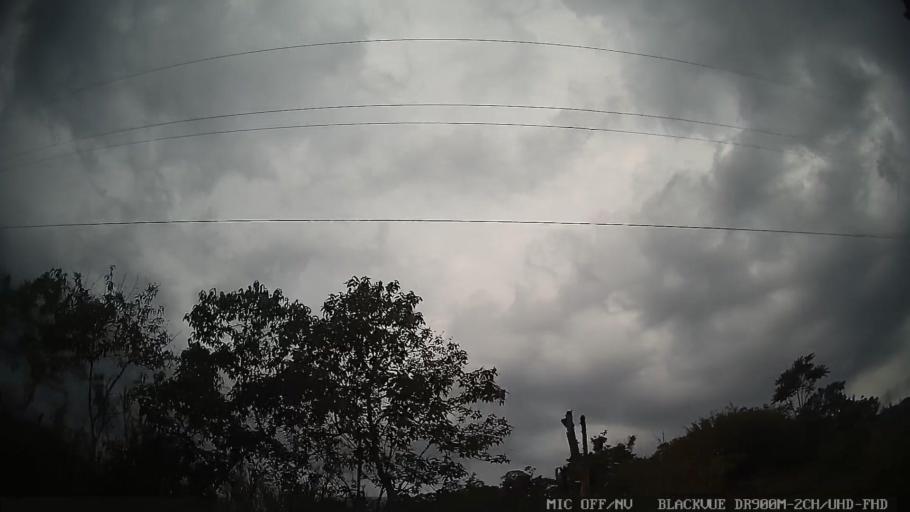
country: BR
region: Sao Paulo
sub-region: Itatiba
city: Itatiba
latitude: -23.0212
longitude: -46.8972
